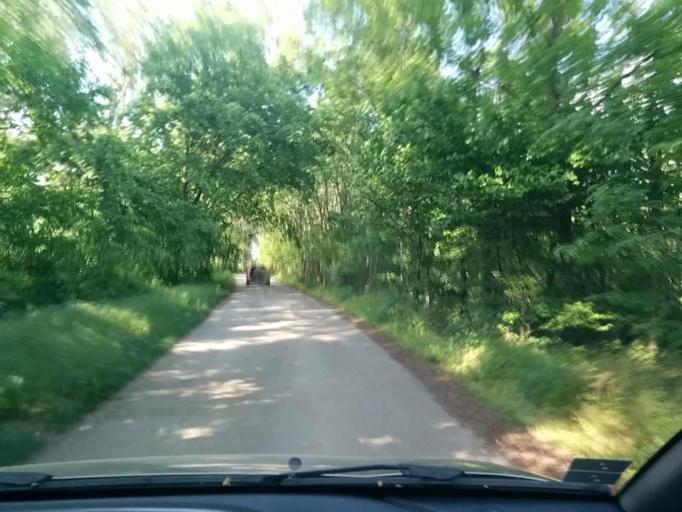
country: SK
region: Bratislavsky
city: Senec
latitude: 48.2009
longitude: 17.5186
